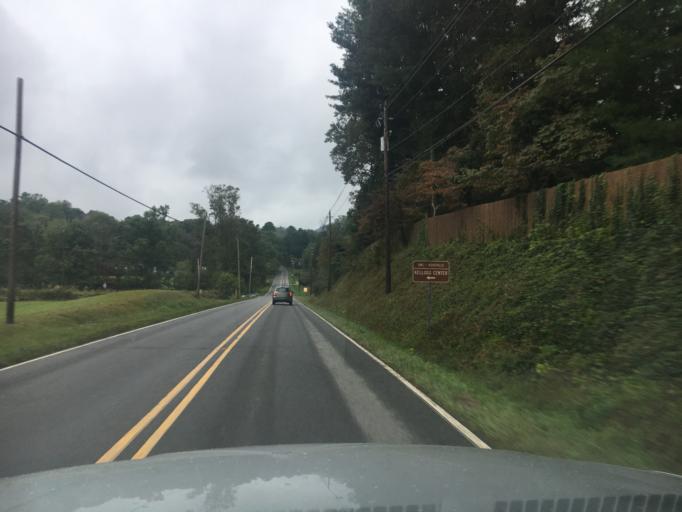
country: US
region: North Carolina
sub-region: Henderson County
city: Horse Shoe
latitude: 35.3366
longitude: -82.5301
